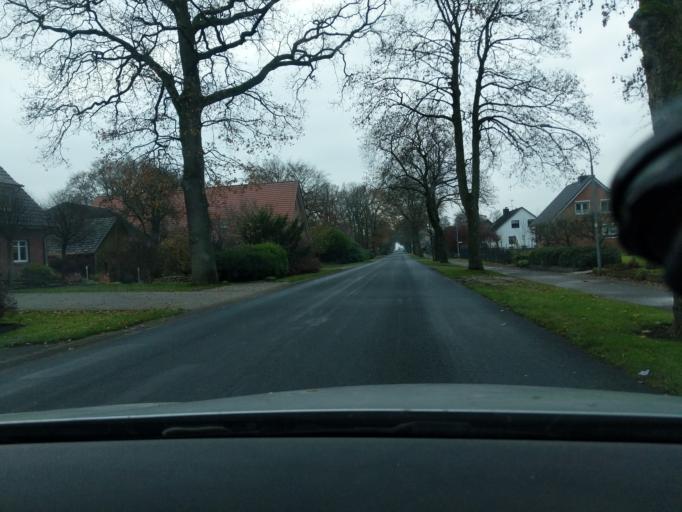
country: DE
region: Lower Saxony
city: Ahlerstedt
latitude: 53.3978
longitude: 9.4894
